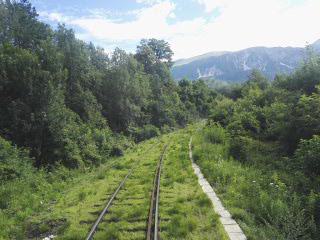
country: SI
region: Bled
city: Zasip
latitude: 46.4022
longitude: 14.0980
